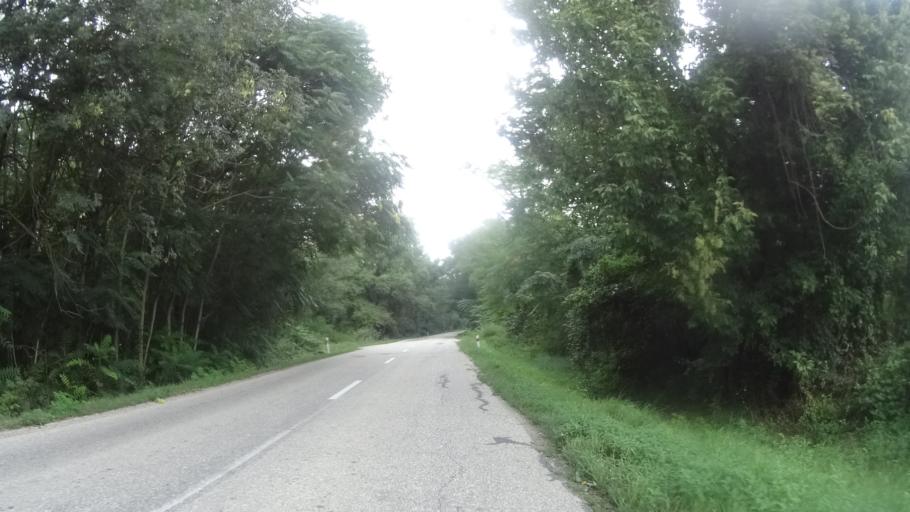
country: SK
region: Trnavsky
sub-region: Okres Dunajska Streda
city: Velky Meder
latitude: 47.7556
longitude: 17.7954
